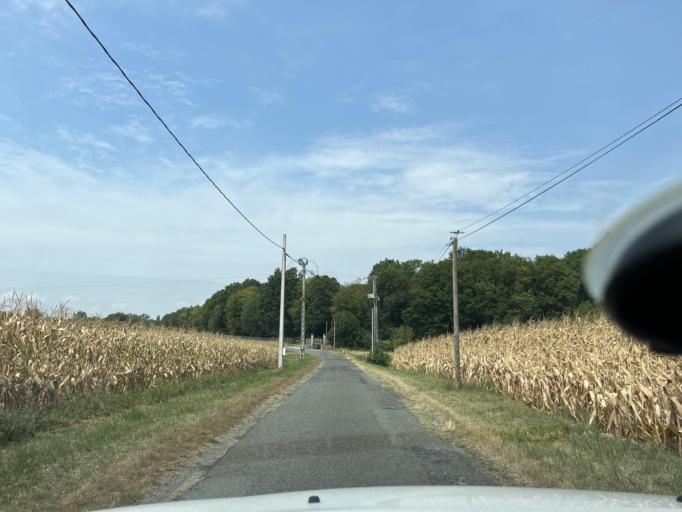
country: FR
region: Poitou-Charentes
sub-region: Departement de la Charente-Maritime
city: Pons
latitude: 45.5987
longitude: -0.5851
